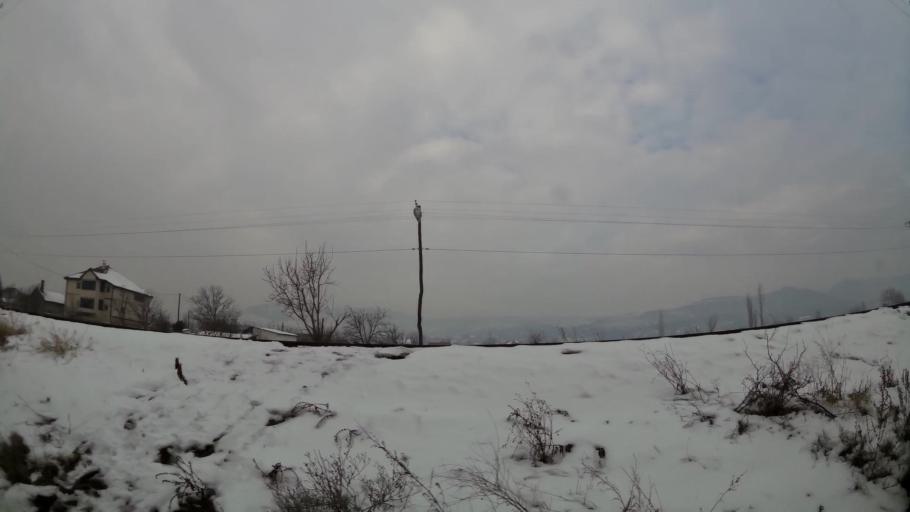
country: MK
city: Kondovo
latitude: 42.0488
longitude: 21.3546
